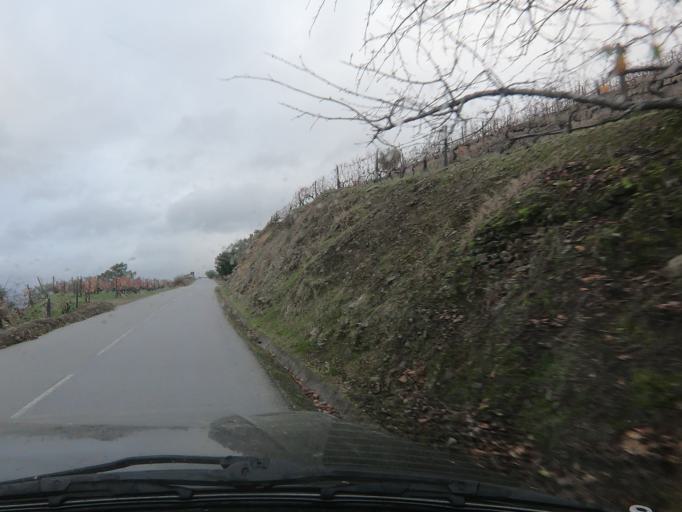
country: PT
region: Vila Real
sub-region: Santa Marta de Penaguiao
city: Santa Marta de Penaguiao
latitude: 41.2076
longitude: -7.7547
